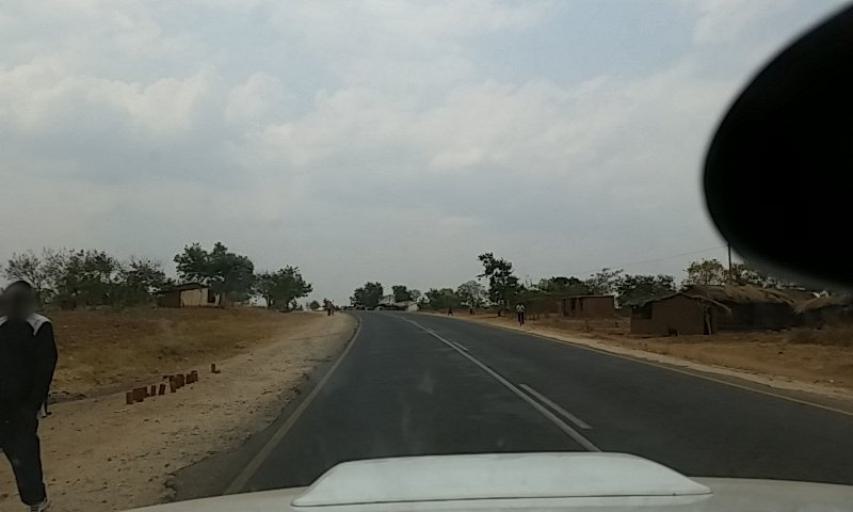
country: MW
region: Central Region
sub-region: Lilongwe District
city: Lilongwe
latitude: -13.8606
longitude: 33.8320
